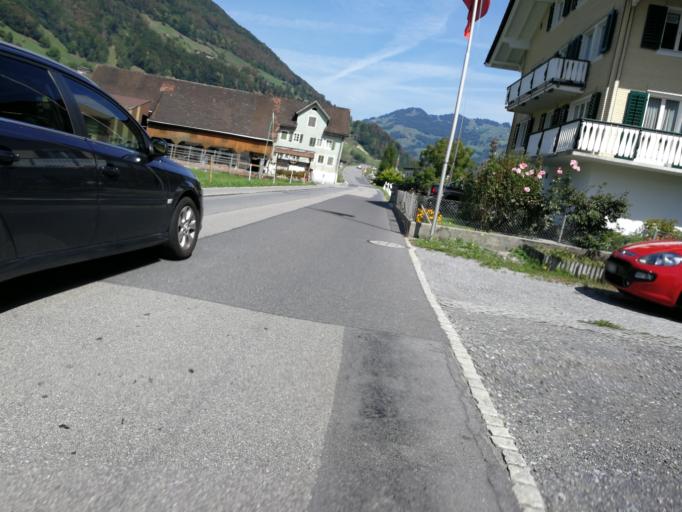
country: CH
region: Schwyz
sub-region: Bezirk Schwyz
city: Ingenbohl
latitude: 47.0047
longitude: 8.6174
